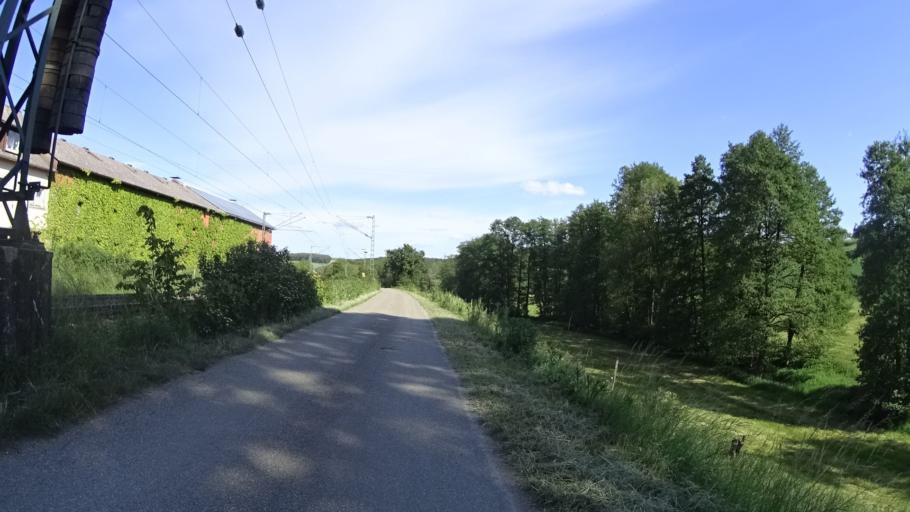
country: DE
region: Baden-Wuerttemberg
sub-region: Regierungsbezirk Stuttgart
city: Buch am Ahorn
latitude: 49.5200
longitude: 9.5860
